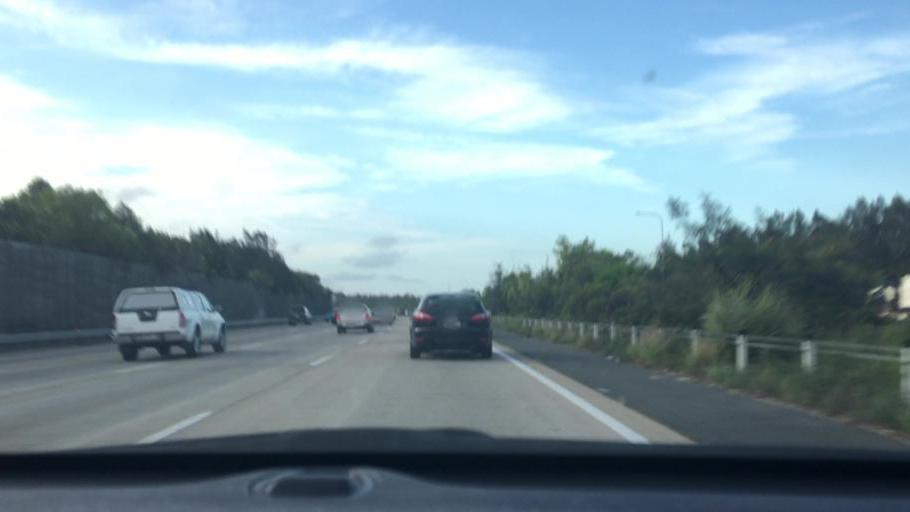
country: AU
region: Queensland
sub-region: Gold Coast
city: Upper Coomera
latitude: -27.9343
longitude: 153.3349
